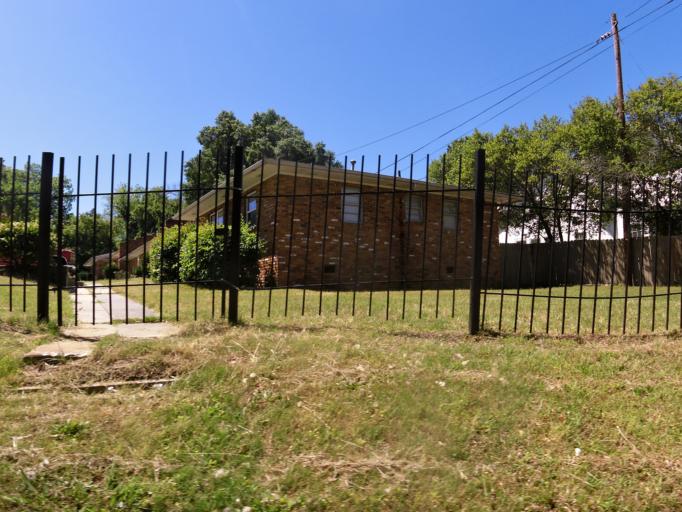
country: US
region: Georgia
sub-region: Richmond County
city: Augusta
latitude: 33.4833
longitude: -82.0248
